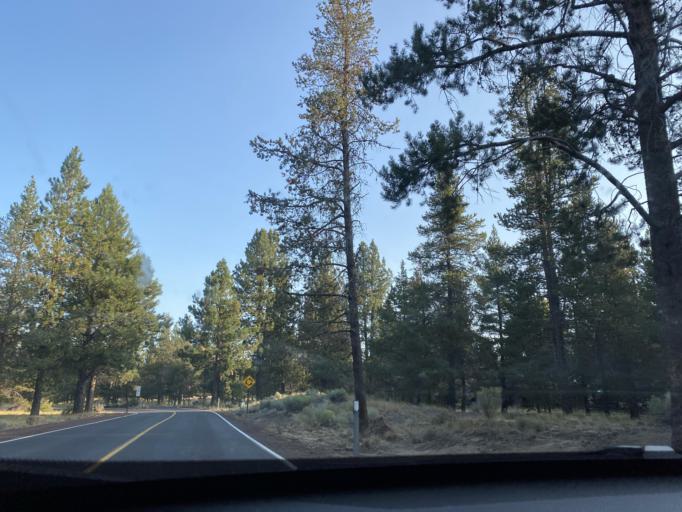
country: US
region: Oregon
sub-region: Deschutes County
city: Sunriver
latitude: 43.8816
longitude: -121.4384
